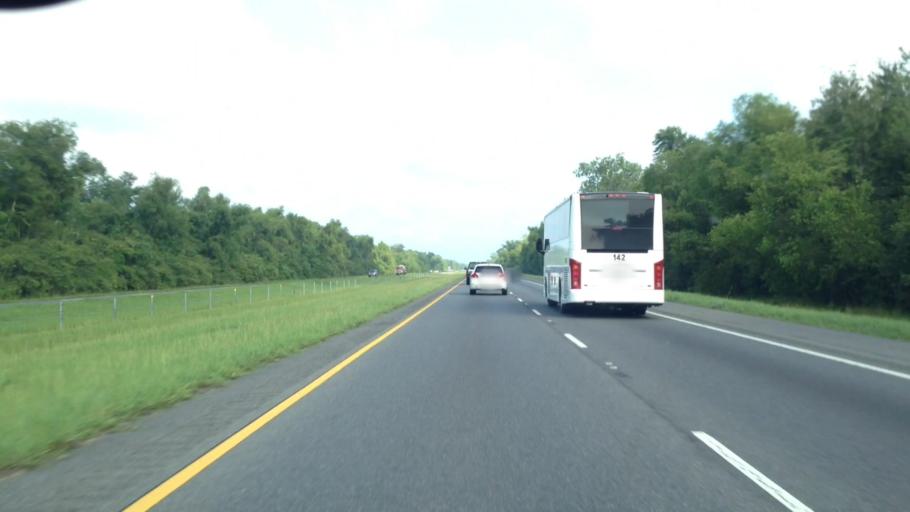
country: US
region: Louisiana
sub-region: Saint James Parish
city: Grand Point
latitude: 30.1366
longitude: -90.7356
